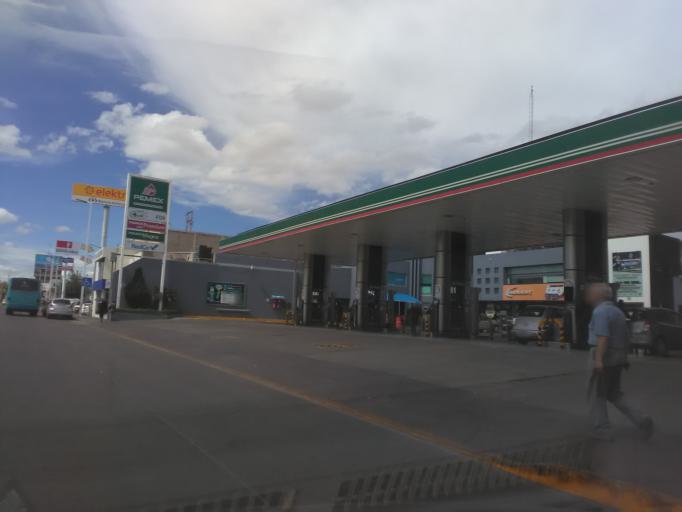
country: MX
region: Durango
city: Victoria de Durango
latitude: 24.0280
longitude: -104.6515
